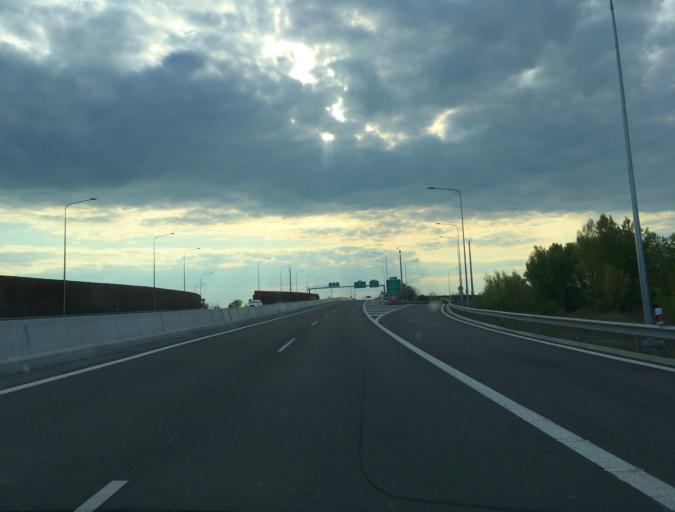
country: AT
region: Burgenland
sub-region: Politischer Bezirk Neusiedl am See
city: Kittsee
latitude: 48.0718
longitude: 17.1064
